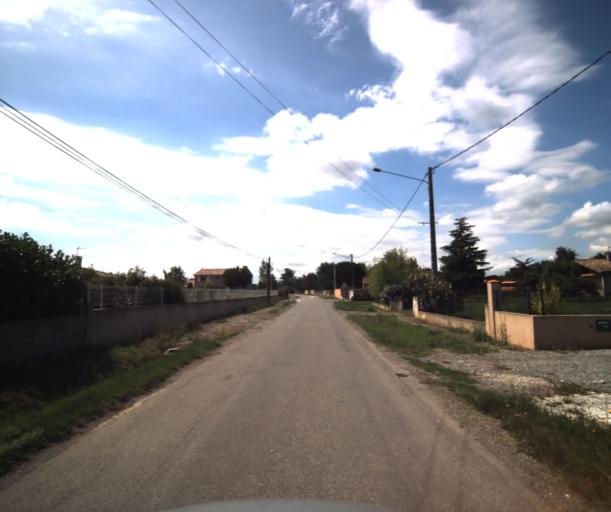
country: FR
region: Midi-Pyrenees
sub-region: Departement de la Haute-Garonne
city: Lacasse
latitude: 43.3896
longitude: 1.2591
